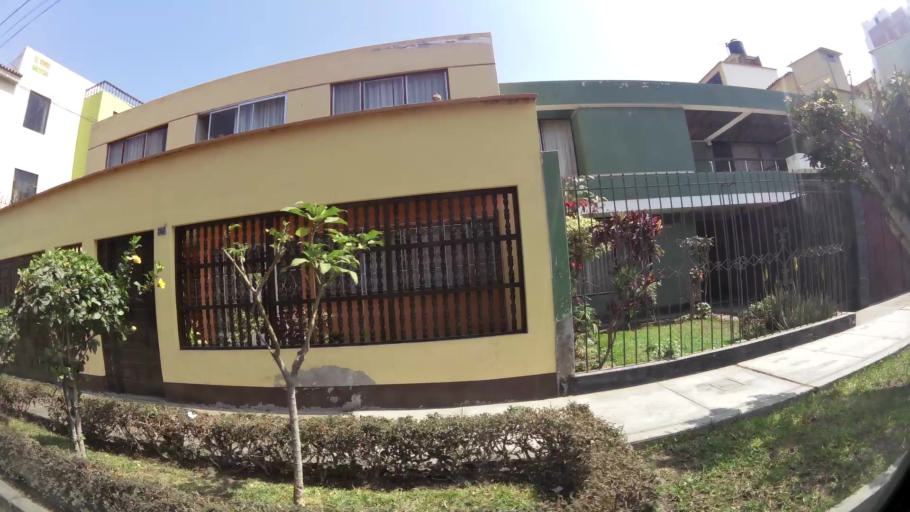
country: PE
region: La Libertad
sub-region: Provincia de Trujillo
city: Buenos Aires
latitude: -8.1341
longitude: -79.0441
